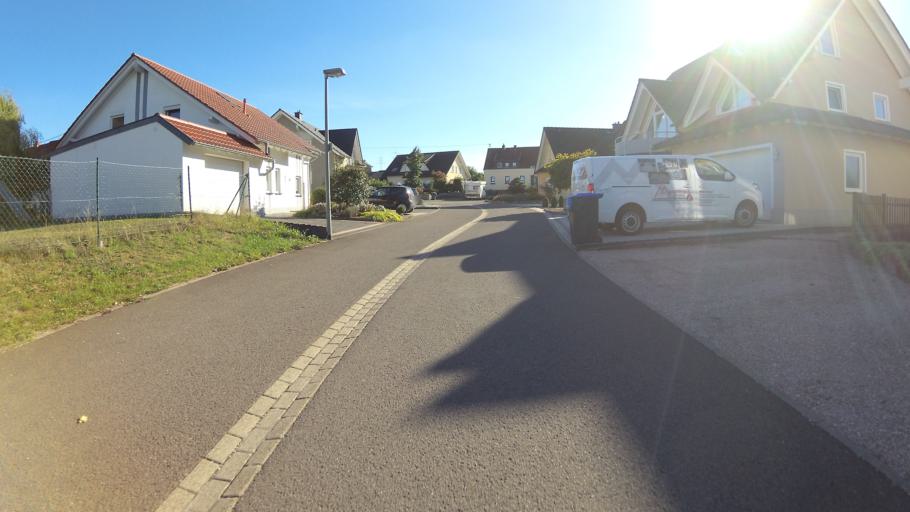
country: DE
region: Saarland
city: Eppelborn
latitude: 49.4082
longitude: 6.9394
